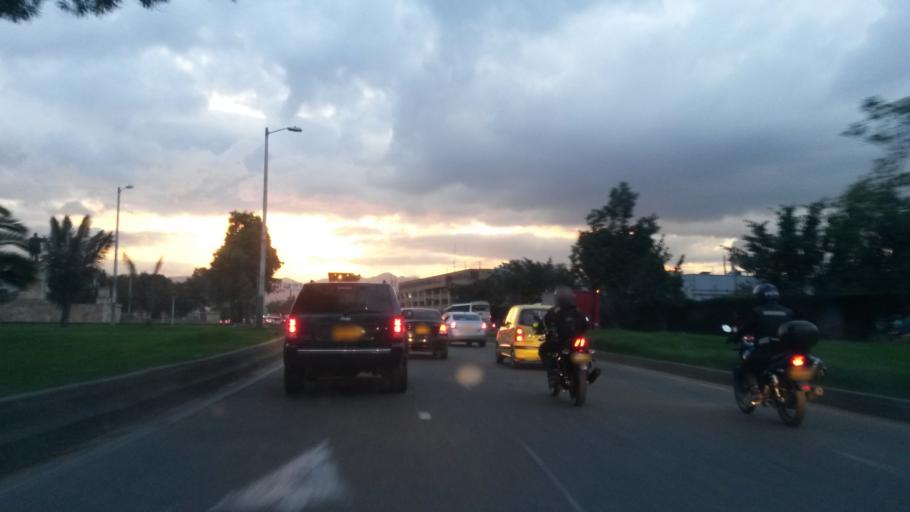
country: CO
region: Cundinamarca
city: Funza
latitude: 4.6880
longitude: -74.1292
